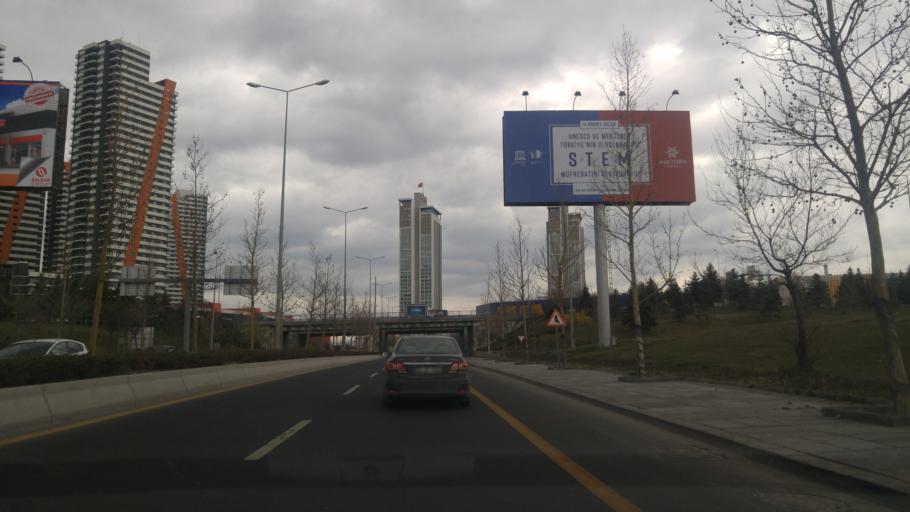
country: TR
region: Ankara
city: Mamak
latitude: 39.8875
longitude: 32.9283
